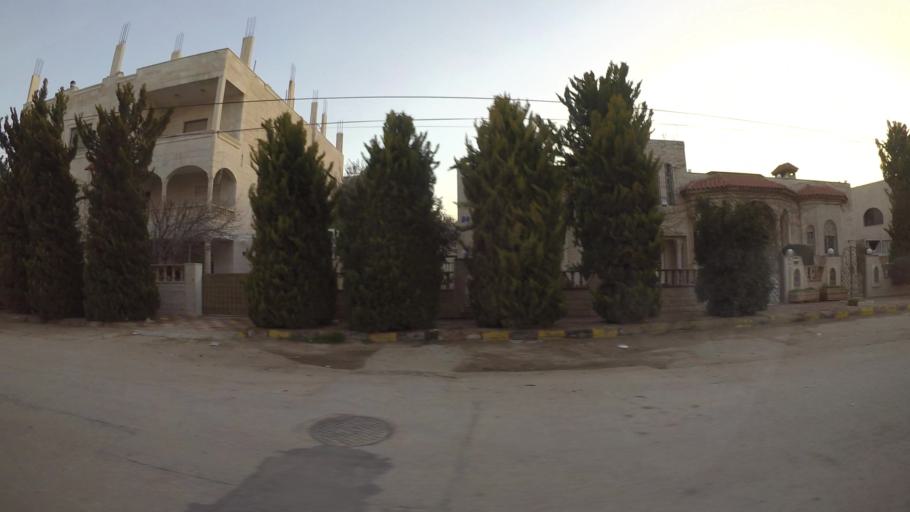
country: JO
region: Amman
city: Al Quwaysimah
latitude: 31.8990
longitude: 35.9291
